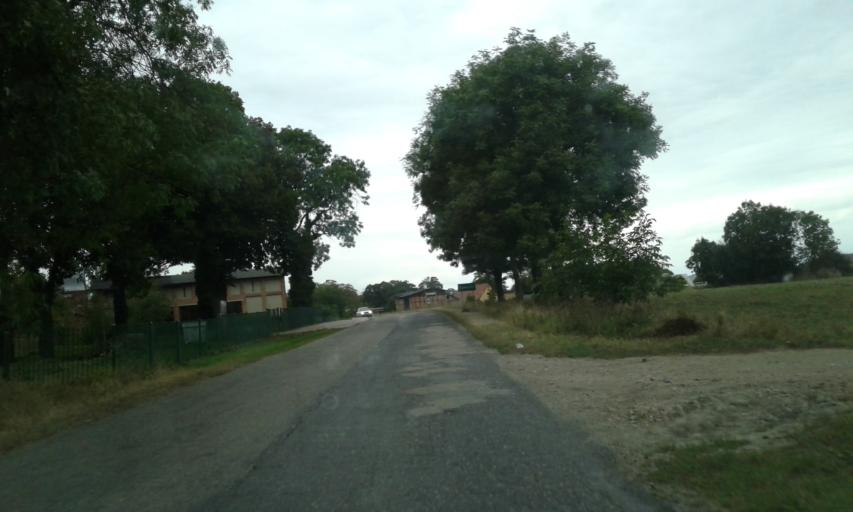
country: PL
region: West Pomeranian Voivodeship
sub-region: Powiat pyrzycki
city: Warnice
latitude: 53.1850
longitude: 15.0190
